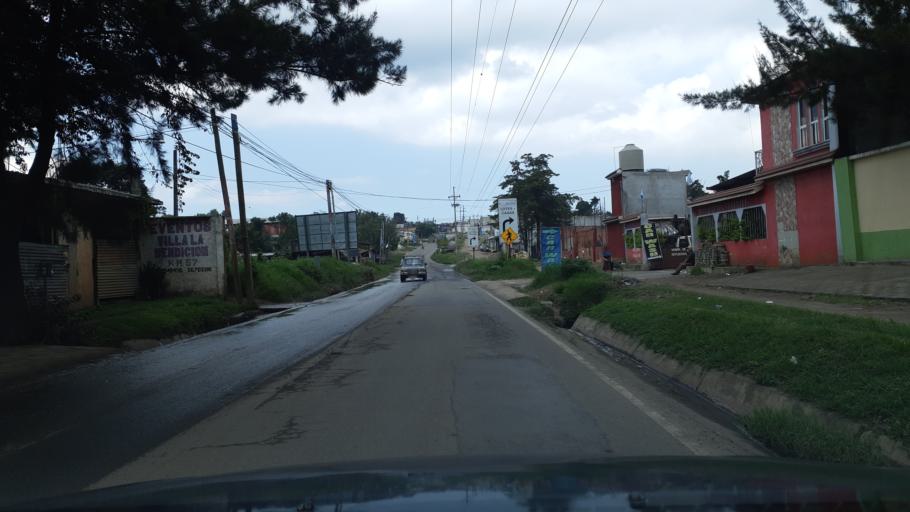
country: GT
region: Chimaltenango
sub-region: Municipio de Chimaltenango
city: Chimaltenango
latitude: 14.6789
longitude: -90.7999
